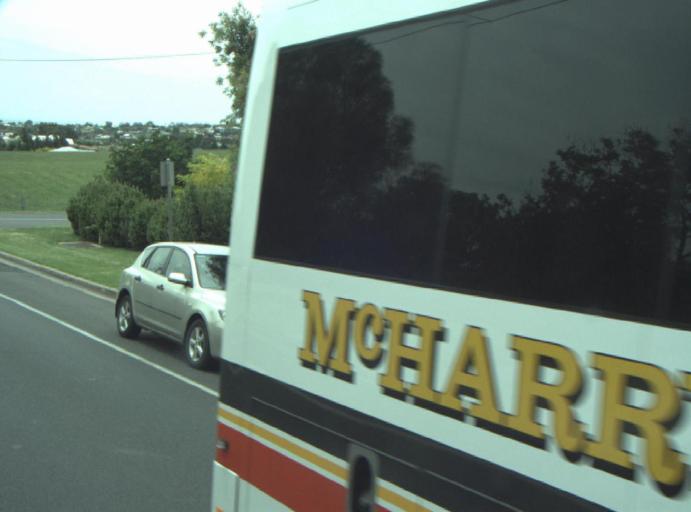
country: AU
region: Victoria
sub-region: Greater Geelong
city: Clifton Springs
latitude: -38.1653
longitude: 144.5723
